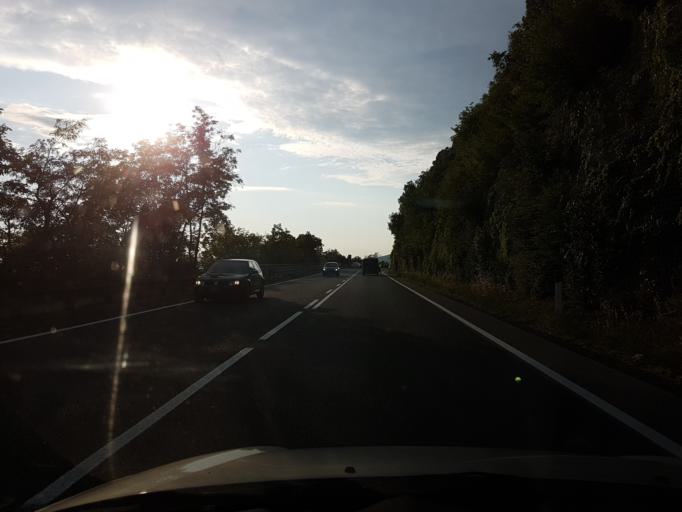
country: IT
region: Friuli Venezia Giulia
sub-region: Provincia di Trieste
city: Sistiana-Visogliano
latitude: 45.7578
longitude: 13.6439
